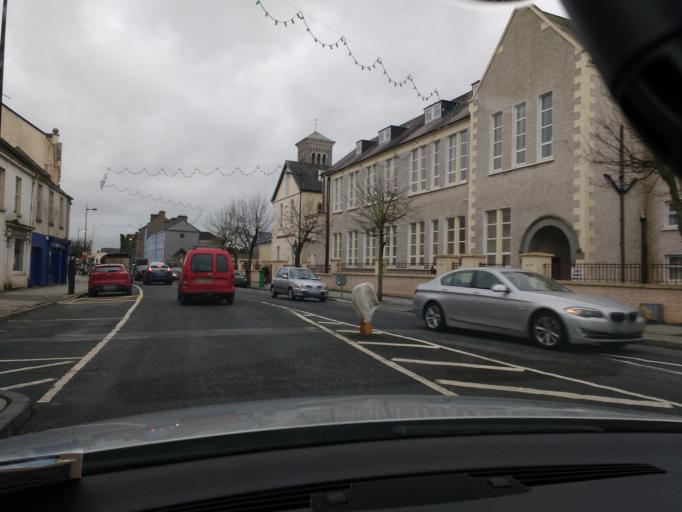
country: IE
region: Munster
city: Thurles
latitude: 52.6801
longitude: -7.8070
